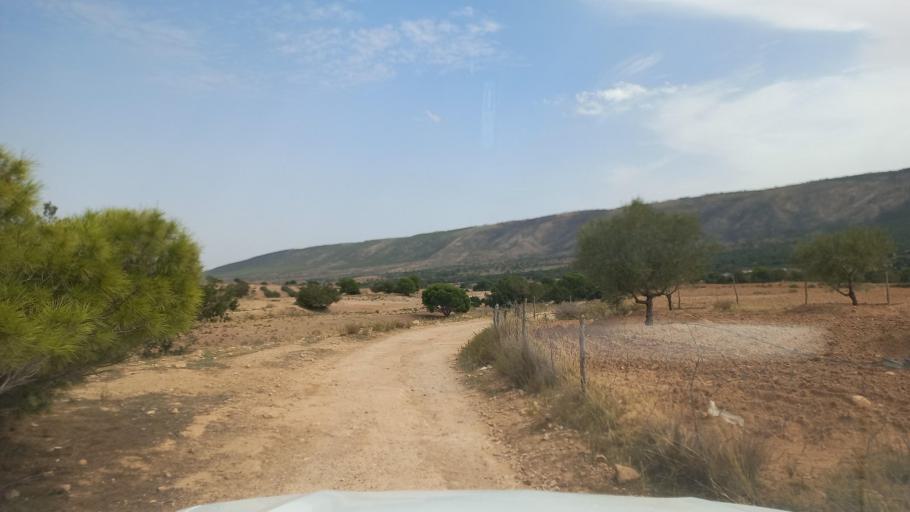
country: TN
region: Al Qasrayn
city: Kasserine
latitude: 35.3709
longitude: 8.8914
